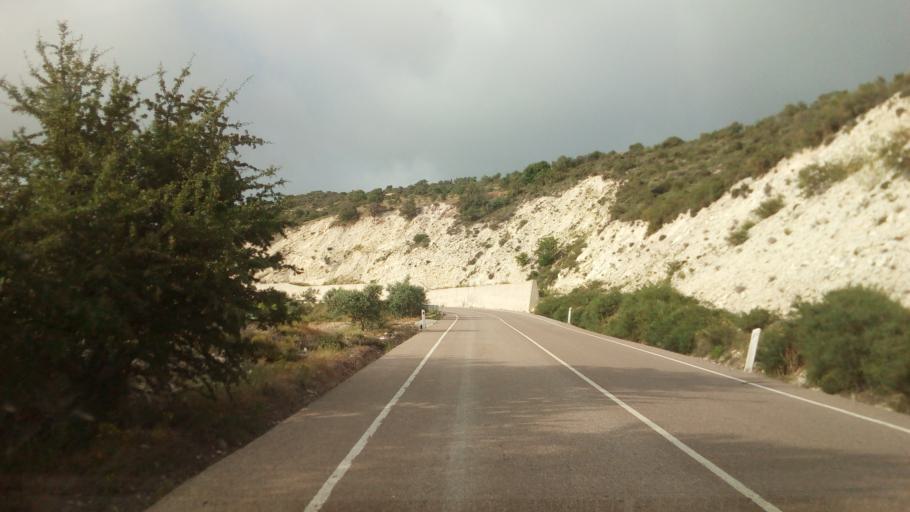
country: CY
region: Limassol
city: Pachna
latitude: 34.8265
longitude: 32.6858
